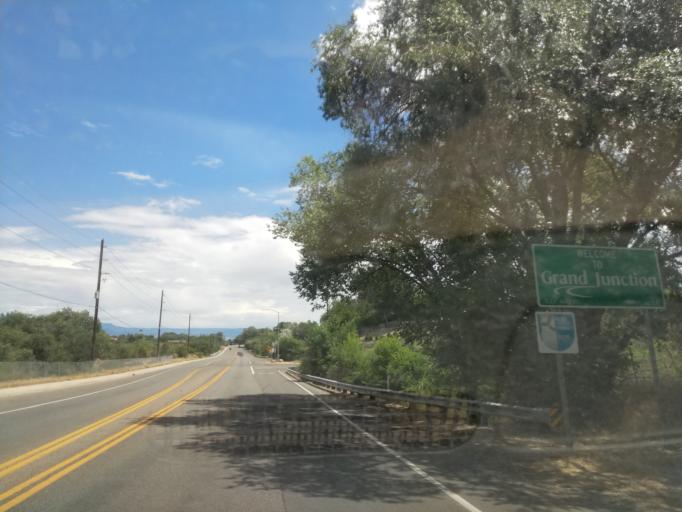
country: US
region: Colorado
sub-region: Mesa County
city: Redlands
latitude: 39.0672
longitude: -108.6033
